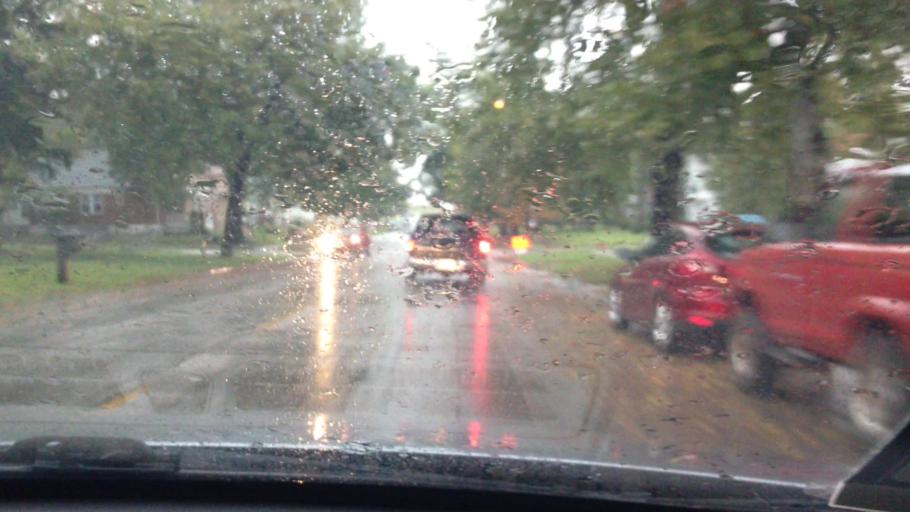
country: US
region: Kansas
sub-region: Leavenworth County
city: Leavenworth
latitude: 39.3254
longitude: -94.9230
